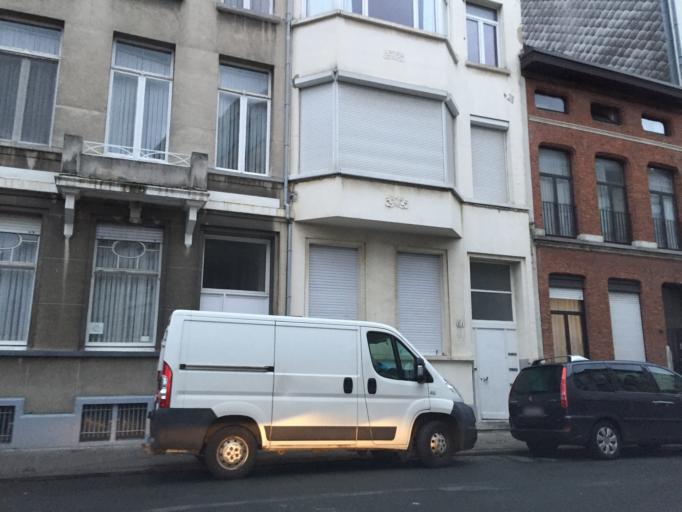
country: BE
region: Flanders
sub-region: Provincie Antwerpen
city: Antwerpen
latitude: 51.2089
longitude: 4.4152
